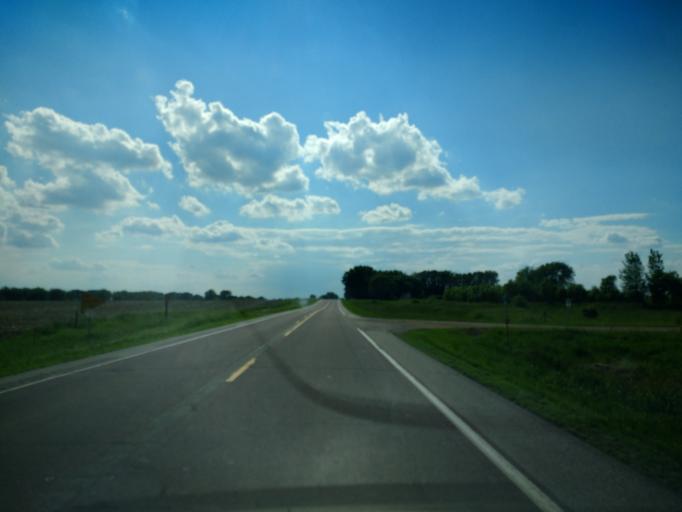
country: US
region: Iowa
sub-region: Clay County
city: Spencer
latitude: 43.1839
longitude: -95.1701
